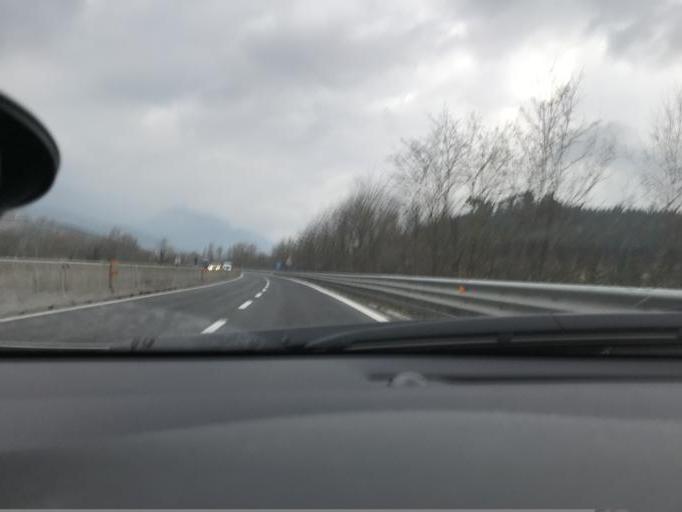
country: IT
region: The Marches
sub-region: Provincia di Ancona
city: Mergo
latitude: 43.4597
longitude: 13.0510
